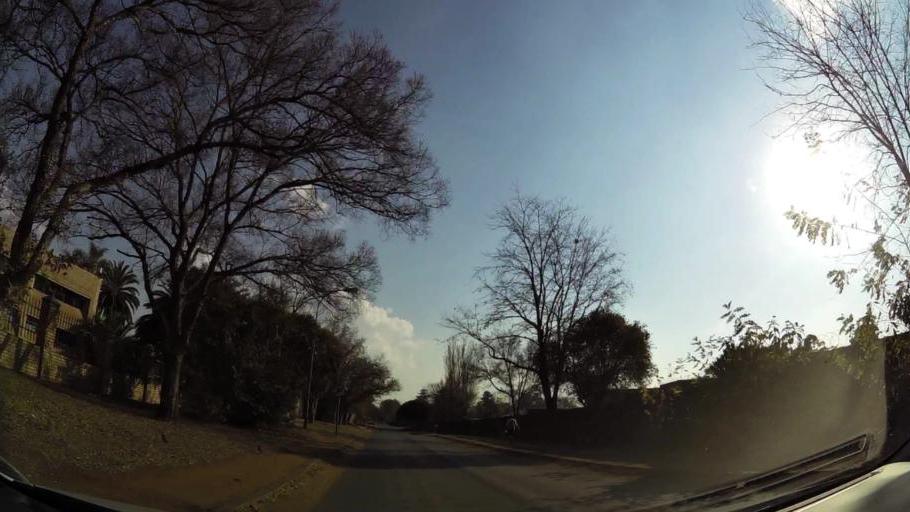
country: ZA
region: Gauteng
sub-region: Ekurhuleni Metropolitan Municipality
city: Tembisa
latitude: -25.9528
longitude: 28.2312
